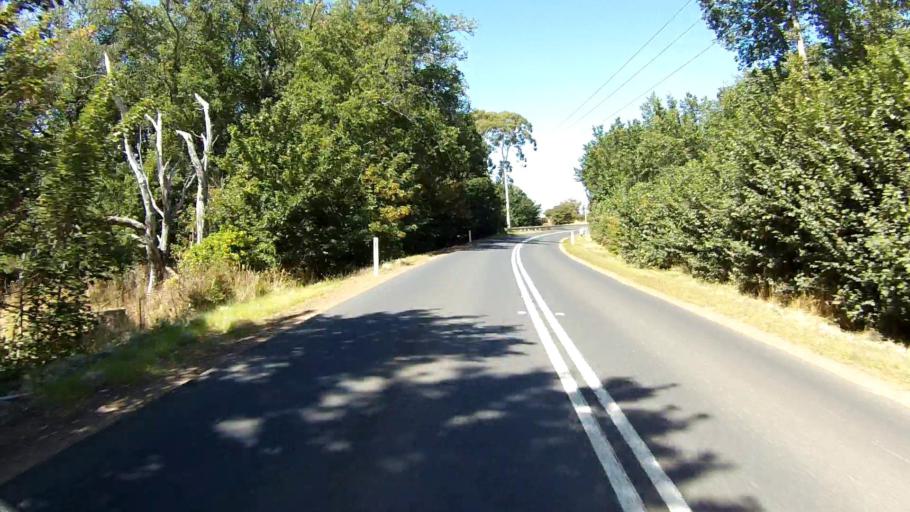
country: AU
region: Tasmania
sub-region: Break O'Day
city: St Helens
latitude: -42.1154
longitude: 148.0600
